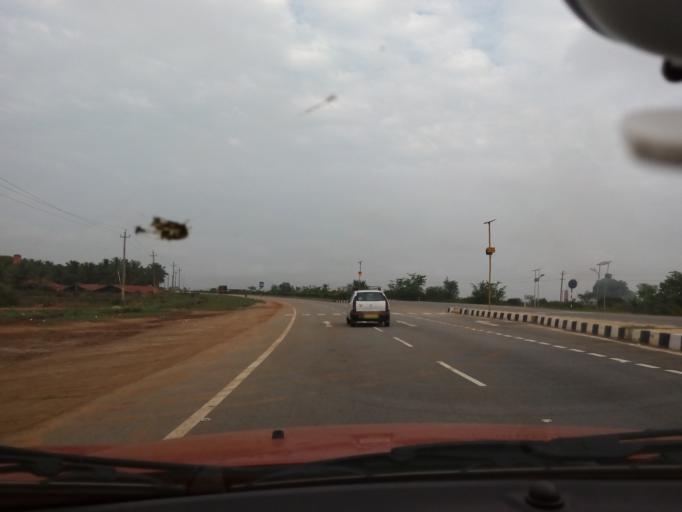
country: IN
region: Karnataka
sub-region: Hassan
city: Shravanabelagola
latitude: 12.9588
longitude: 76.5913
